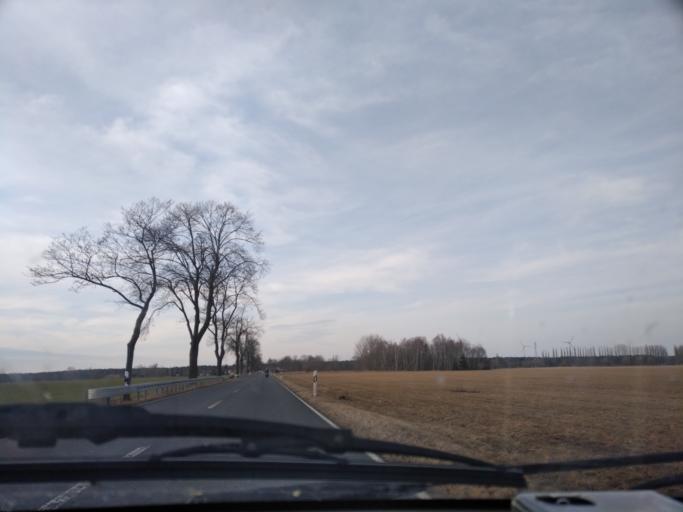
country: DE
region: Saxony-Anhalt
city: Holzdorf
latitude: 51.8319
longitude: 13.1544
